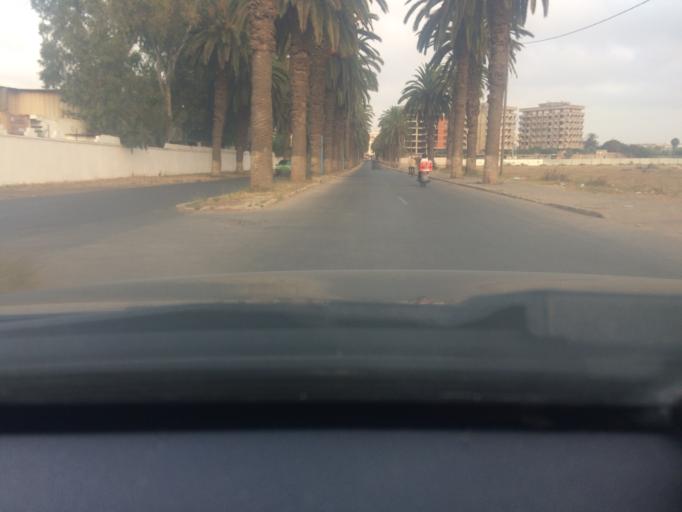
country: MA
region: Grand Casablanca
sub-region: Mohammedia
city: Mohammedia
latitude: 33.6950
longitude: -7.3969
